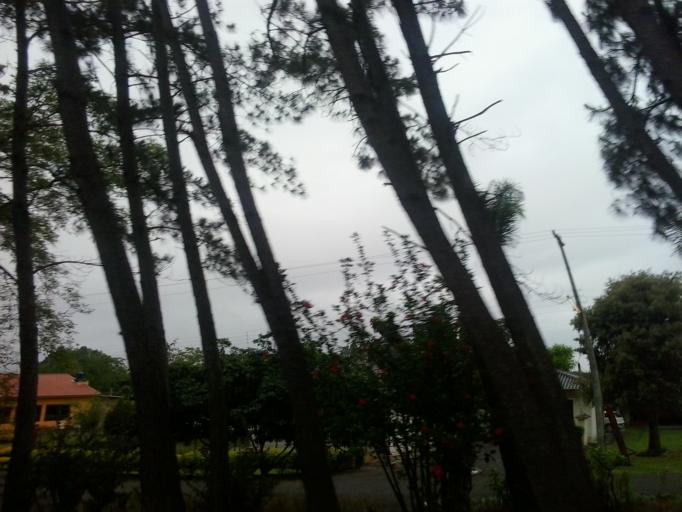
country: BR
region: Rio Grande do Sul
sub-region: Candelaria
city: Candelaria
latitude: -29.7155
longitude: -53.2449
